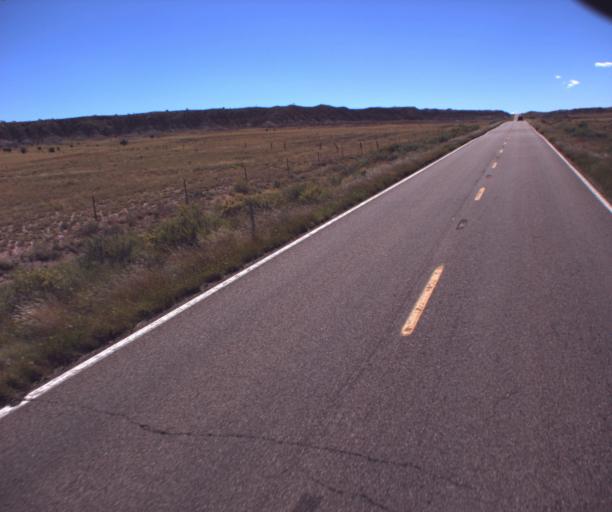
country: US
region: Arizona
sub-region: Apache County
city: Saint Johns
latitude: 34.6653
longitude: -109.2910
